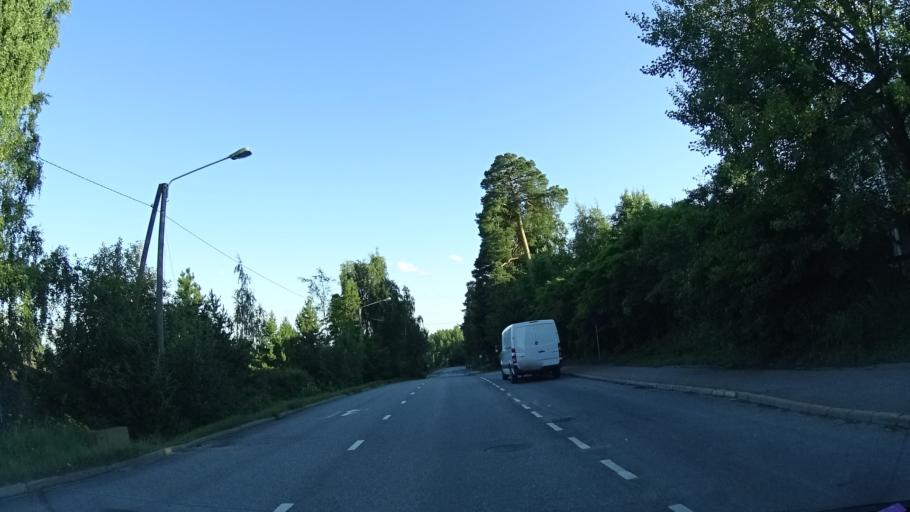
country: FI
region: Uusimaa
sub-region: Helsinki
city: Teekkarikylae
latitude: 60.2768
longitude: 24.8750
